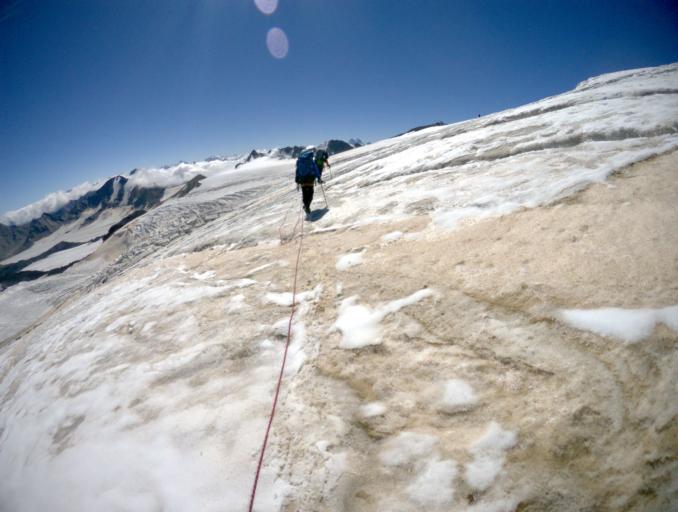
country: RU
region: Kabardino-Balkariya
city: Terskol
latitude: 43.3630
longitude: 42.4988
